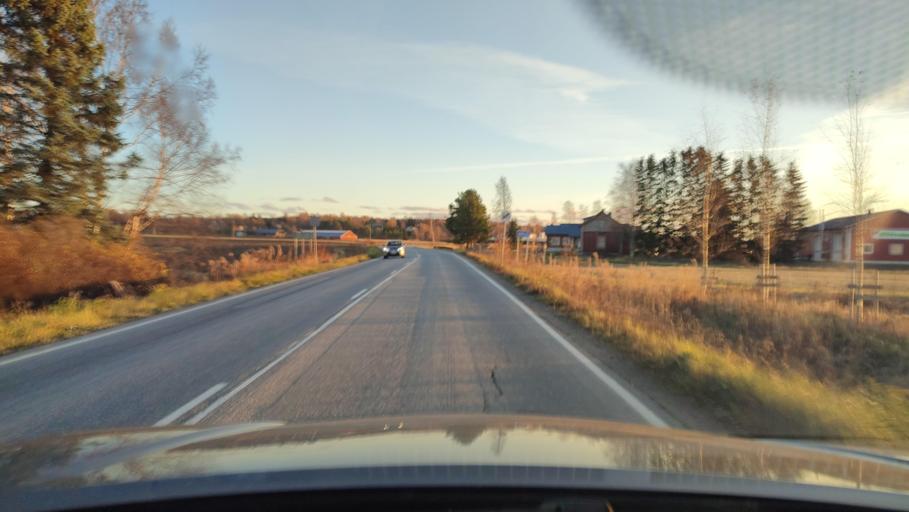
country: FI
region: Ostrobothnia
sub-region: Sydosterbotten
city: Naerpes
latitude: 62.4407
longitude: 21.3512
